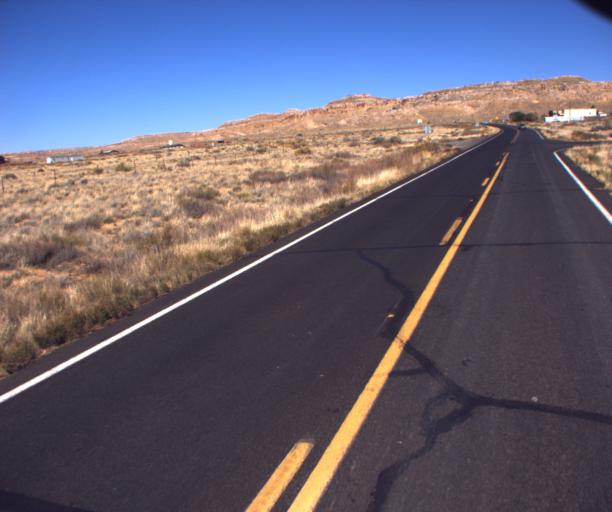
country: US
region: Arizona
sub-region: Navajo County
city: First Mesa
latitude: 35.7877
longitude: -110.4985
